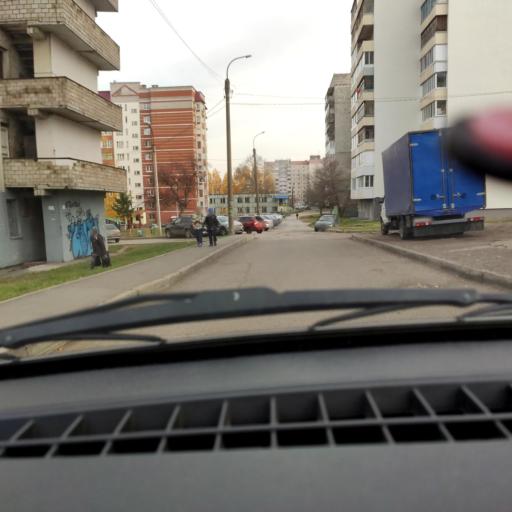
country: RU
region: Bashkortostan
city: Ufa
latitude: 54.8198
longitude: 56.1155
